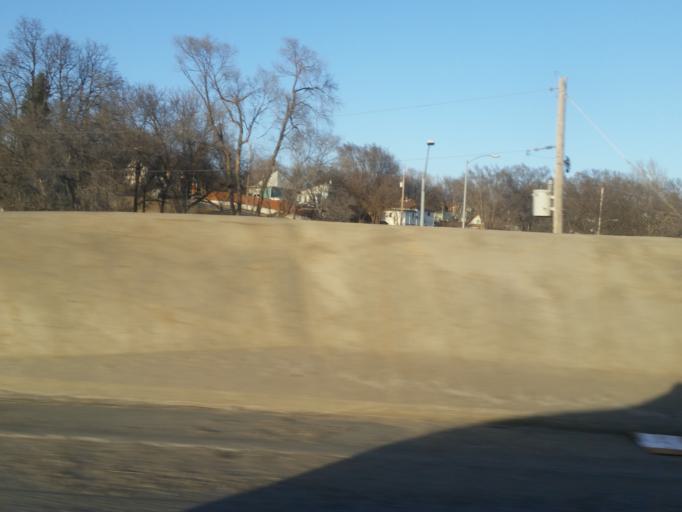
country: US
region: Nebraska
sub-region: Douglas County
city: Omaha
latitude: 41.1971
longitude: -95.9429
